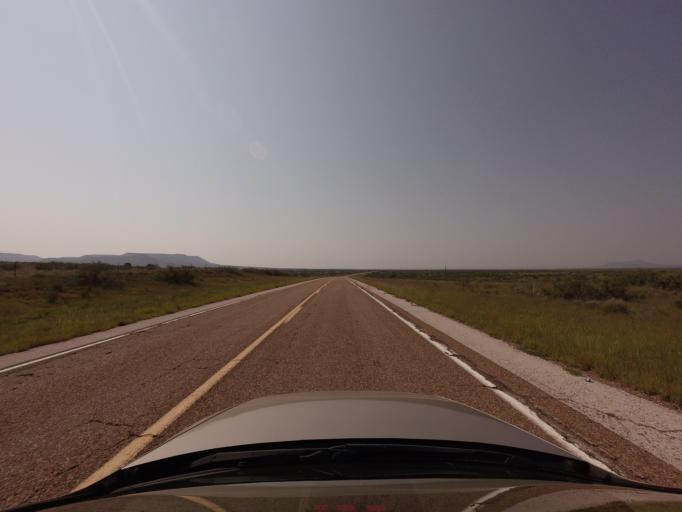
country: US
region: New Mexico
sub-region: Quay County
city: Tucumcari
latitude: 35.0229
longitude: -103.7376
